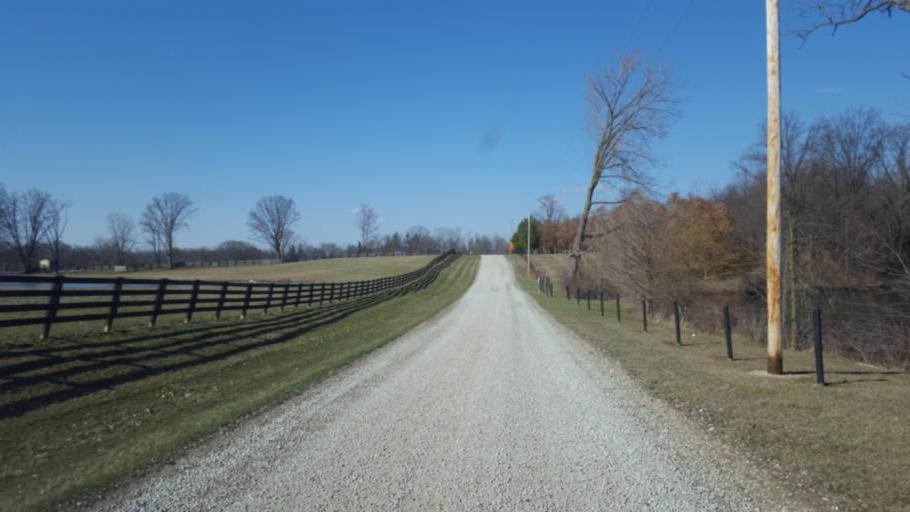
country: US
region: Ohio
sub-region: Morrow County
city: Mount Gilead
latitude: 40.5323
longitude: -82.7780
